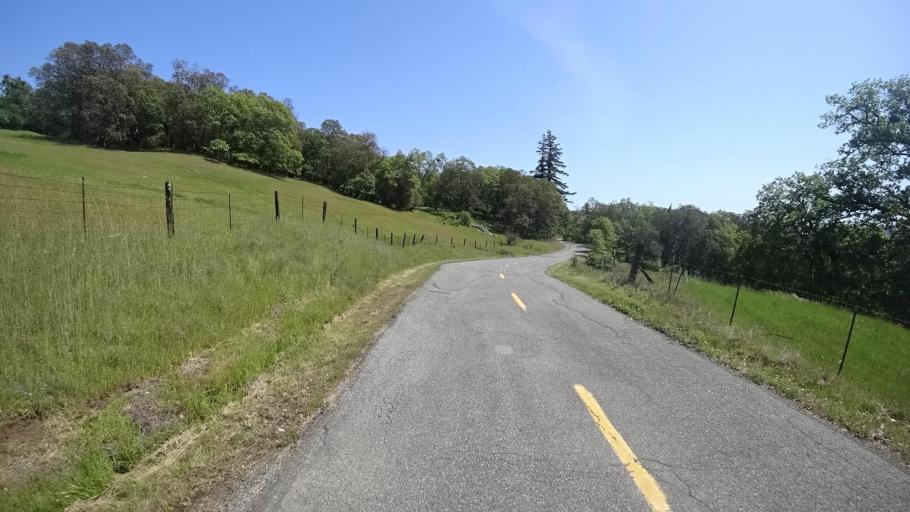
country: US
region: California
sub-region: Humboldt County
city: Redway
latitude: 40.2590
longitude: -123.6257
